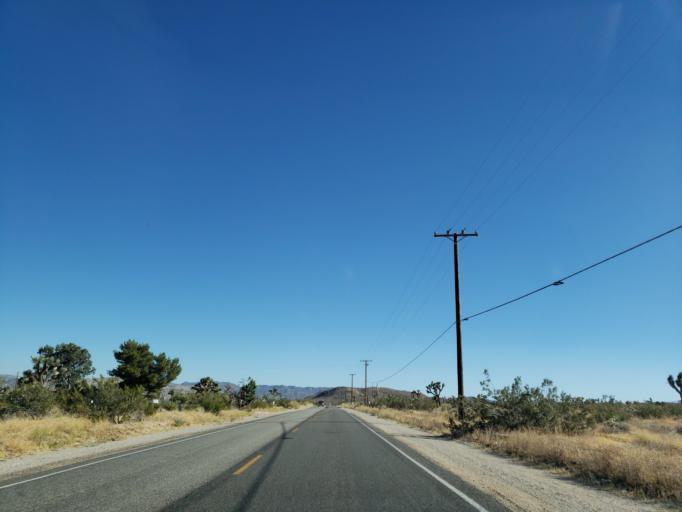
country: US
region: California
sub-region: San Bernardino County
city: Yucca Valley
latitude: 34.1796
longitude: -116.3871
